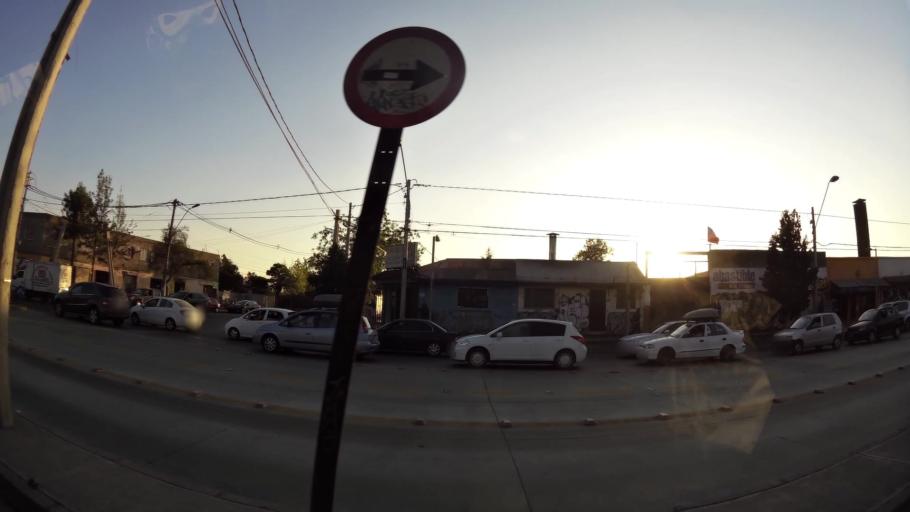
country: CL
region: Santiago Metropolitan
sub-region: Provincia de Santiago
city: Santiago
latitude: -33.5155
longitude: -70.6247
